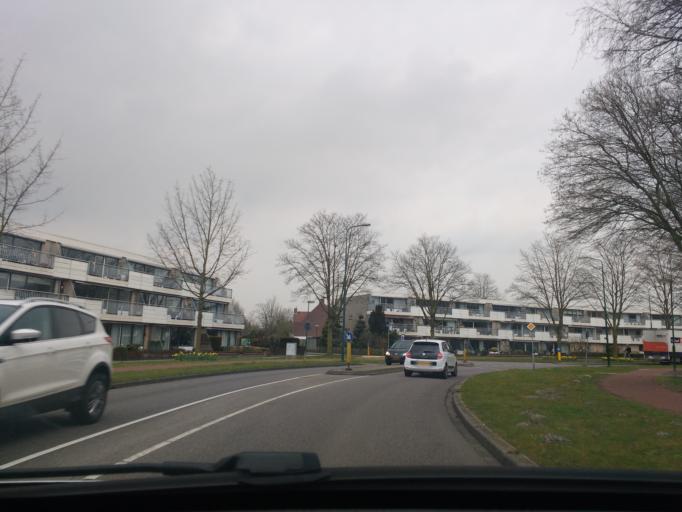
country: NL
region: Utrecht
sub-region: Gemeente Veenendaal
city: Veenendaal
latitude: 52.0315
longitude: 5.5387
